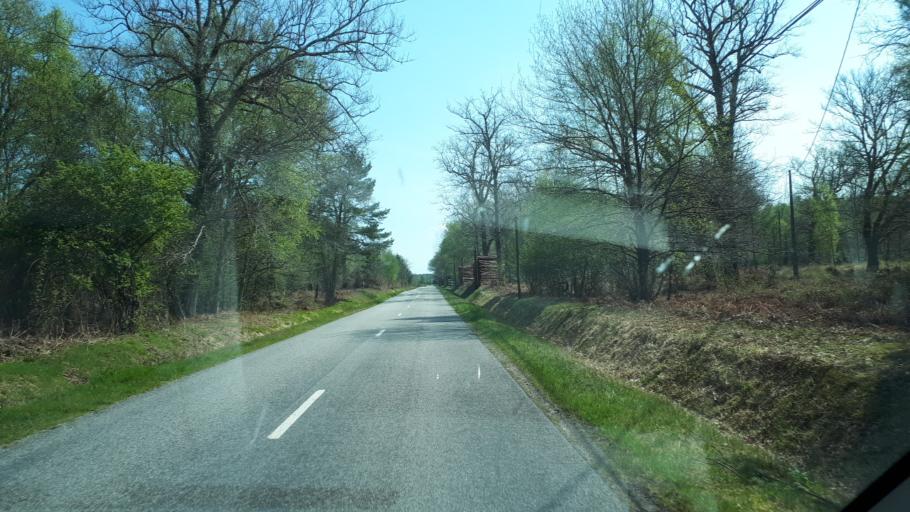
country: FR
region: Centre
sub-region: Departement du Loir-et-Cher
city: Theillay
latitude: 47.3136
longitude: 2.0765
